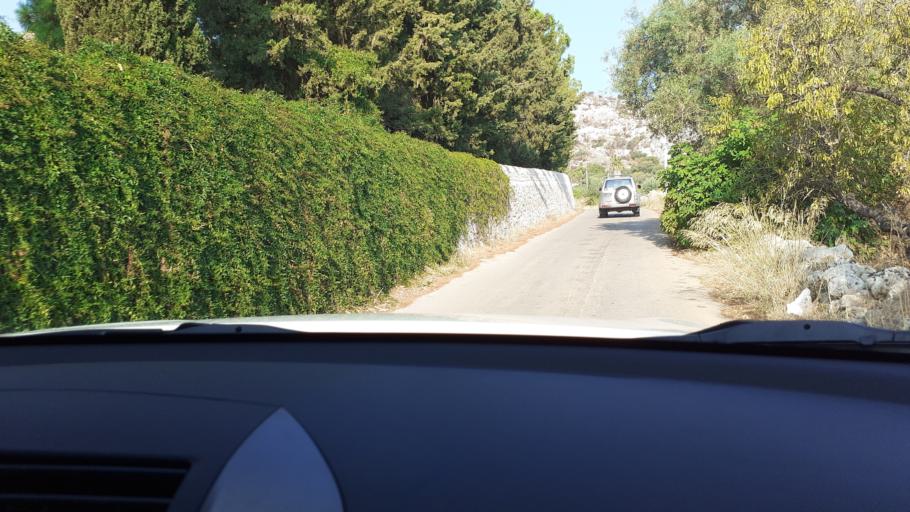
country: IT
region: Sicily
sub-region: Provincia di Siracusa
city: Cassibile
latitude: 36.9788
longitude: 15.1757
